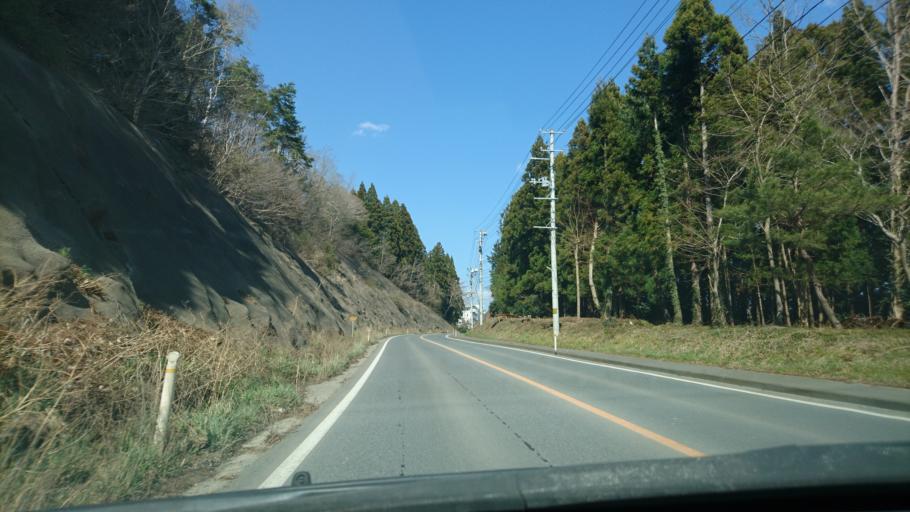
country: JP
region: Miyagi
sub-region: Oshika Gun
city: Onagawa Cho
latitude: 38.6554
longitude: 141.4470
